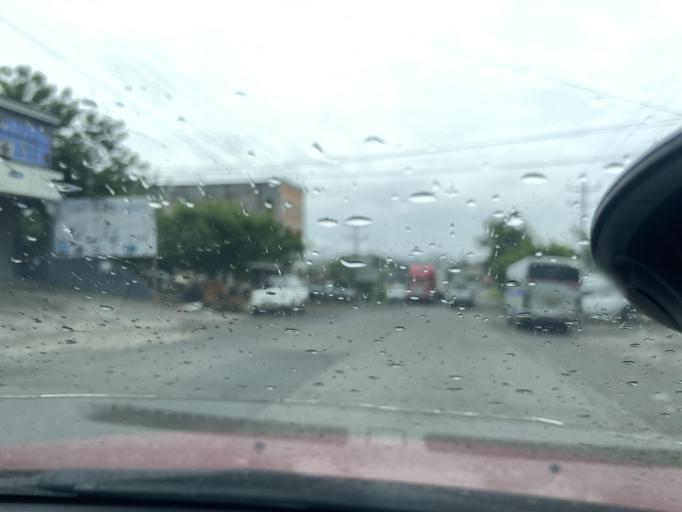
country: SV
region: La Union
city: Santa Rosa de Lima
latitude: 13.6216
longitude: -87.8969
